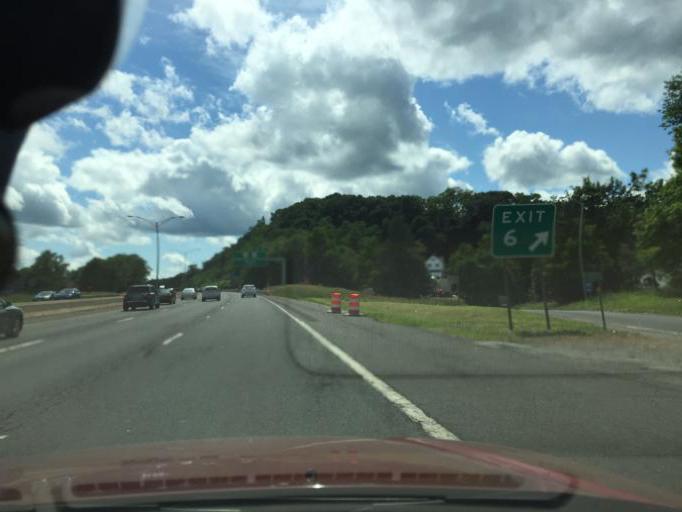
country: US
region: Connecticut
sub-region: Fairfield County
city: Danbury
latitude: 41.4109
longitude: -73.4533
